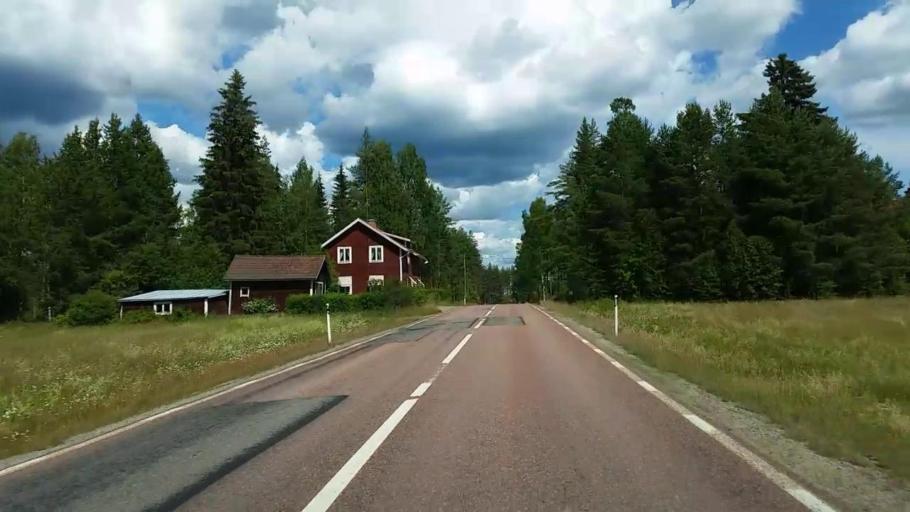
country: SE
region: Gaevleborg
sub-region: Ovanakers Kommun
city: Edsbyn
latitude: 61.3565
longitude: 15.6950
